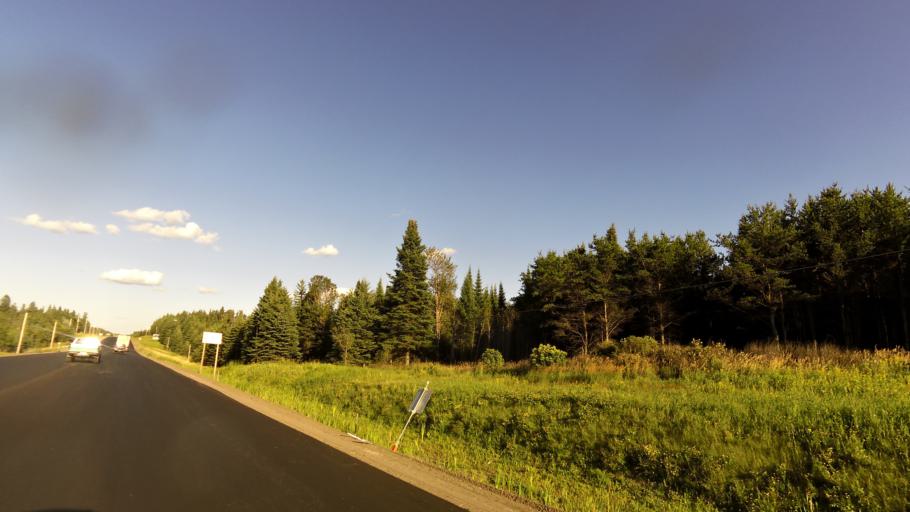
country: CA
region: Ontario
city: Dryden
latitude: 49.8151
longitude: -92.8877
